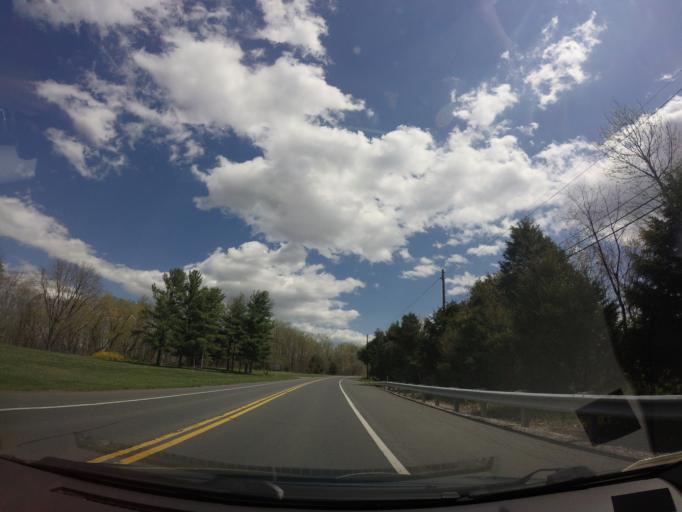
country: US
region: West Virginia
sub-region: Jefferson County
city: Shepherdstown
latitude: 39.4385
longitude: -77.7948
